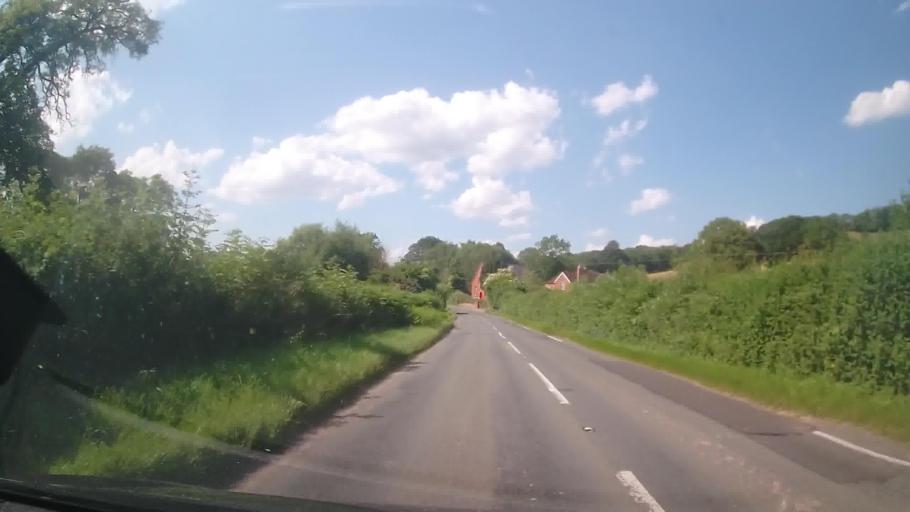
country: GB
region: England
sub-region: Herefordshire
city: Brockhampton
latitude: 52.0018
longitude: -2.5901
